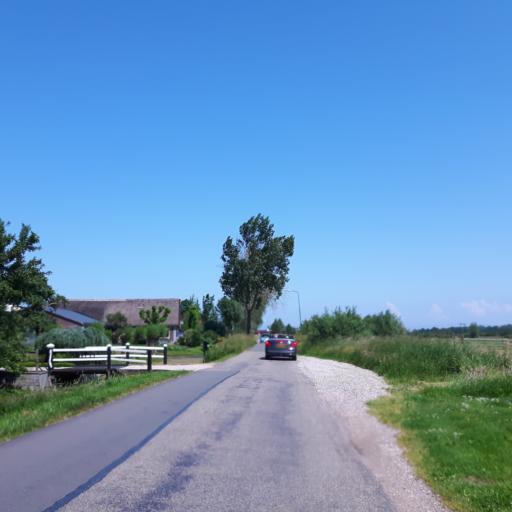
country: NL
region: Utrecht
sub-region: Stichtse Vecht
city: Spechtenkamp
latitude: 52.1280
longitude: 4.9667
